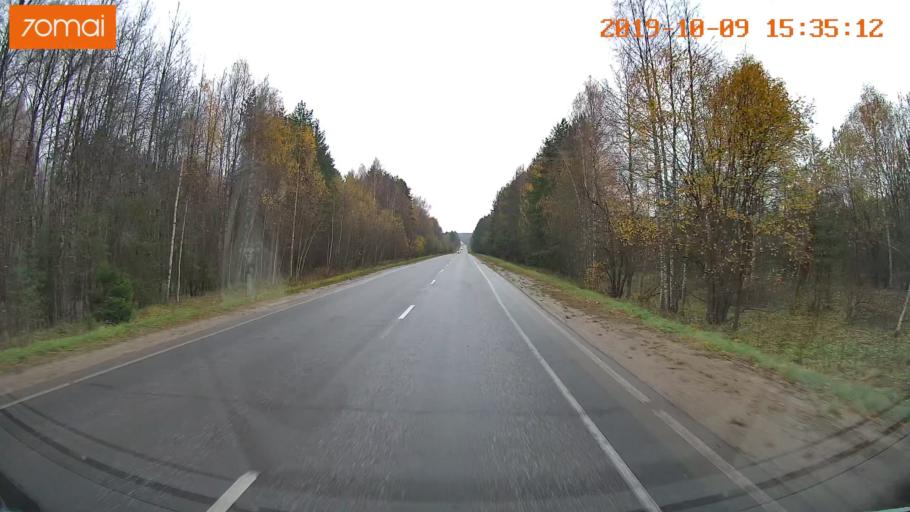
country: RU
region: Kostroma
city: Oktyabr'skiy
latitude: 57.9345
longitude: 41.2322
